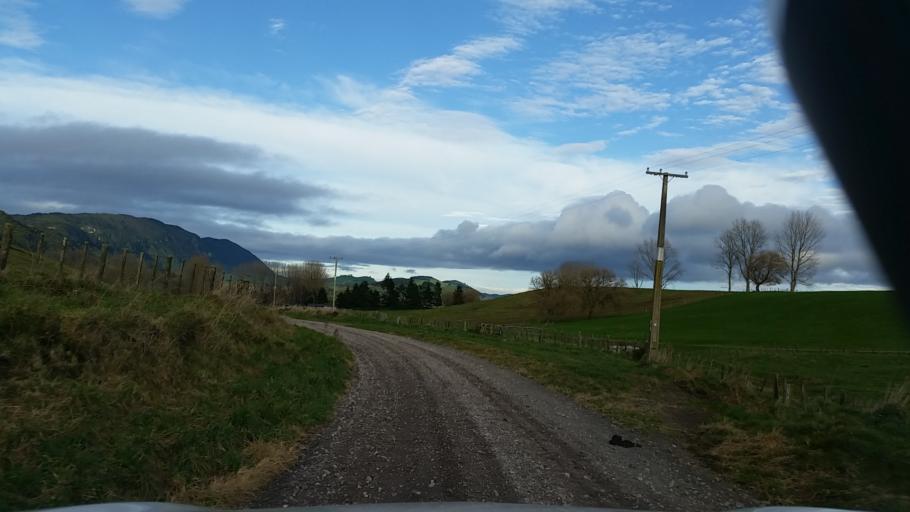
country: NZ
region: Bay of Plenty
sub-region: Rotorua District
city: Rotorua
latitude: -38.3176
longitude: 176.3001
